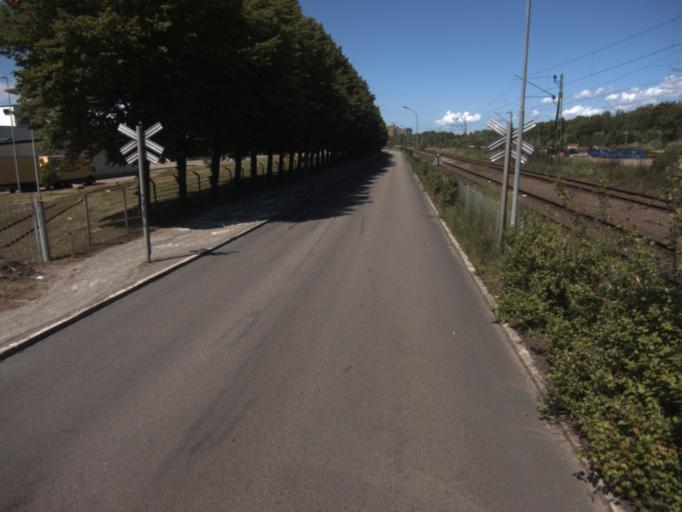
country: SE
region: Skane
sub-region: Helsingborg
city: Helsingborg
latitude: 56.0173
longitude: 12.7344
